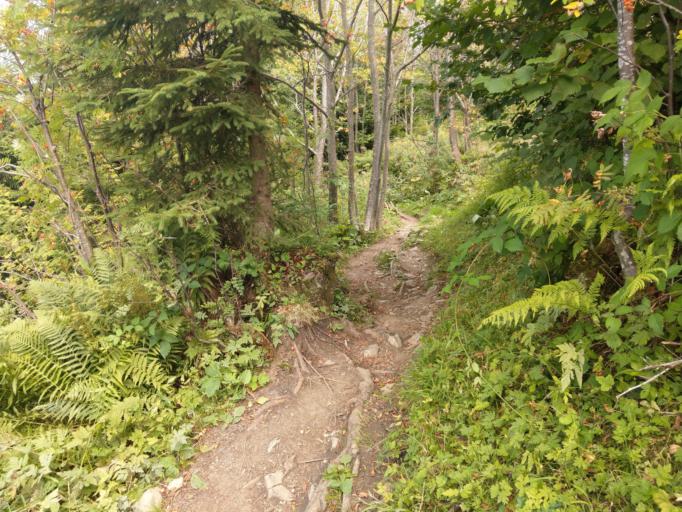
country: DE
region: Bavaria
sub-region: Swabia
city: Nesselwang
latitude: 47.6028
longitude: 10.5011
